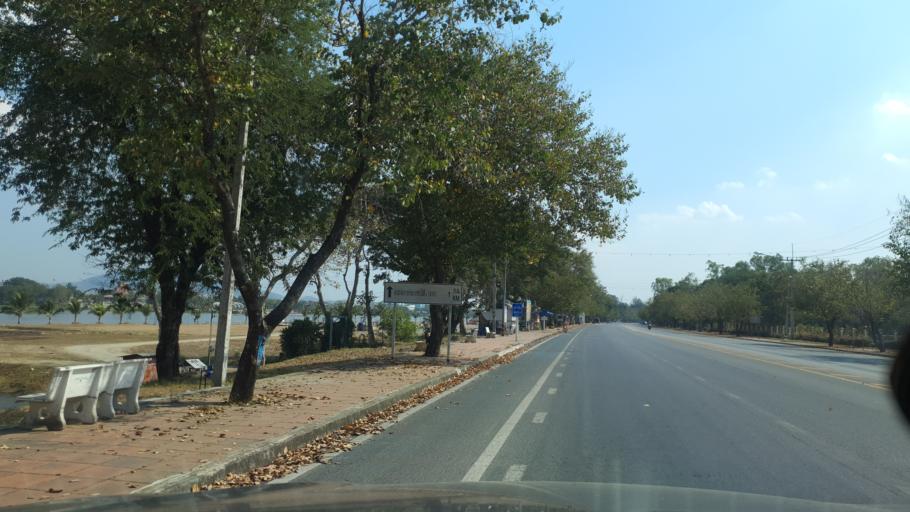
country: TH
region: Tak
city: Tak
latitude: 16.8815
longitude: 99.1140
